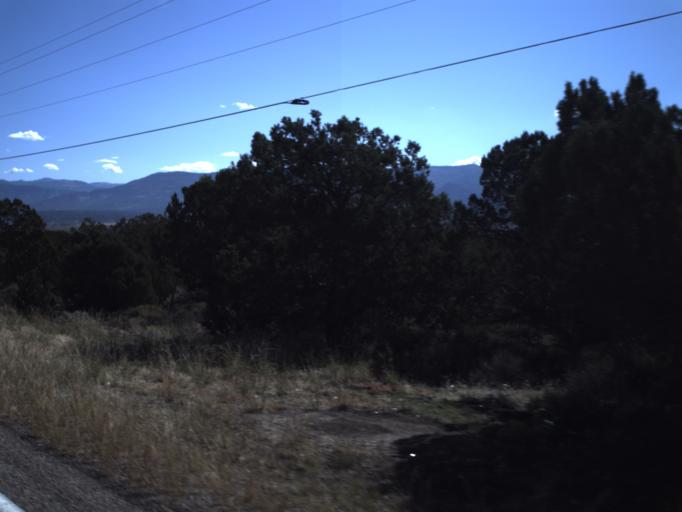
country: US
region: Utah
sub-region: Iron County
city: Cedar City
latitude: 37.6414
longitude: -113.2542
